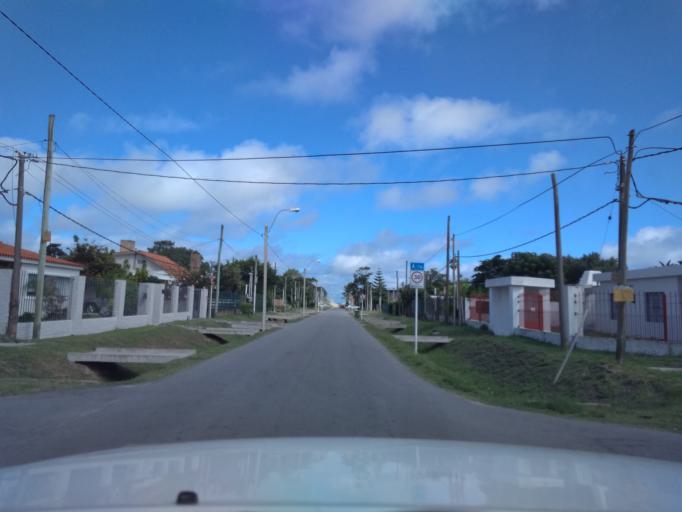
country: UY
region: Canelones
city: Barra de Carrasco
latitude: -34.8376
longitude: -55.9692
